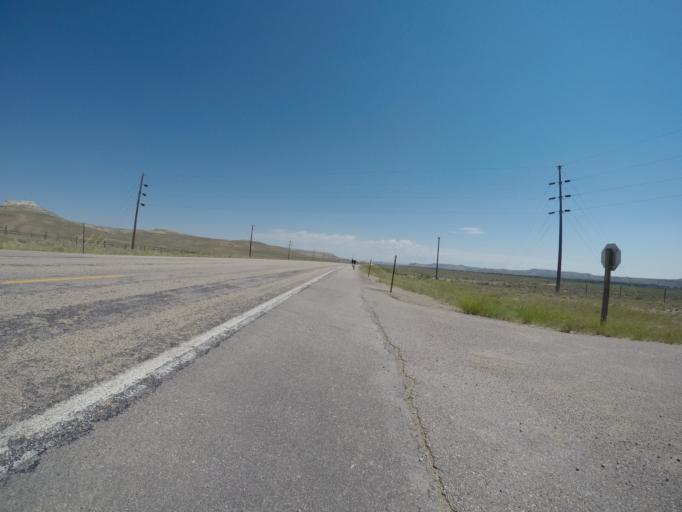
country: US
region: Wyoming
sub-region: Sublette County
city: Marbleton
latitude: 42.3716
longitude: -110.1482
